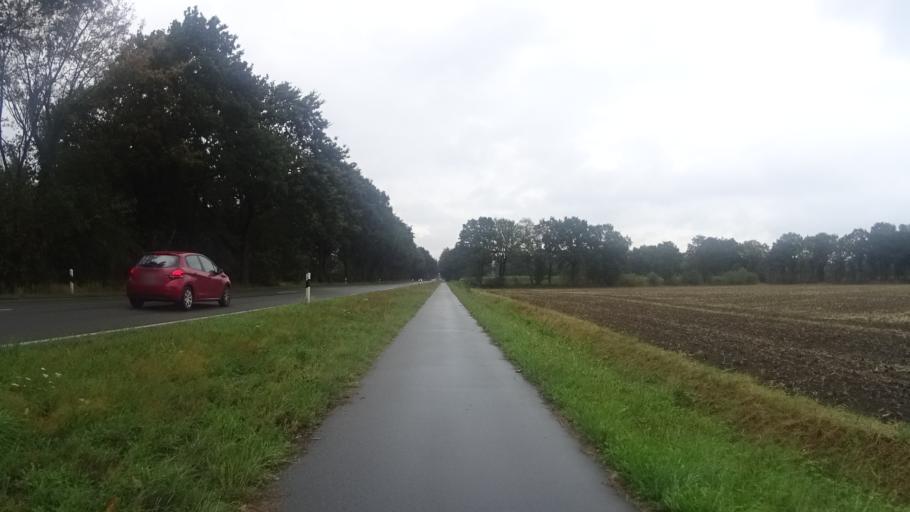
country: DE
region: Lower Saxony
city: Holtland
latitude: 53.2840
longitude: 7.5791
